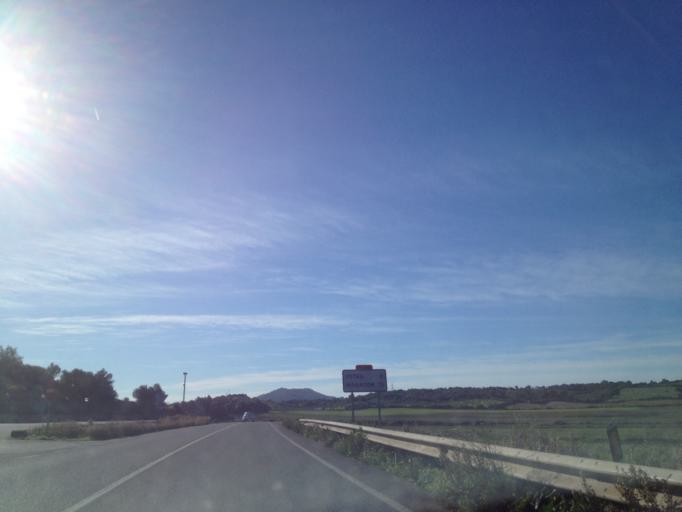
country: ES
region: Balearic Islands
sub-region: Illes Balears
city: Ariany
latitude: 39.6452
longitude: 3.1001
